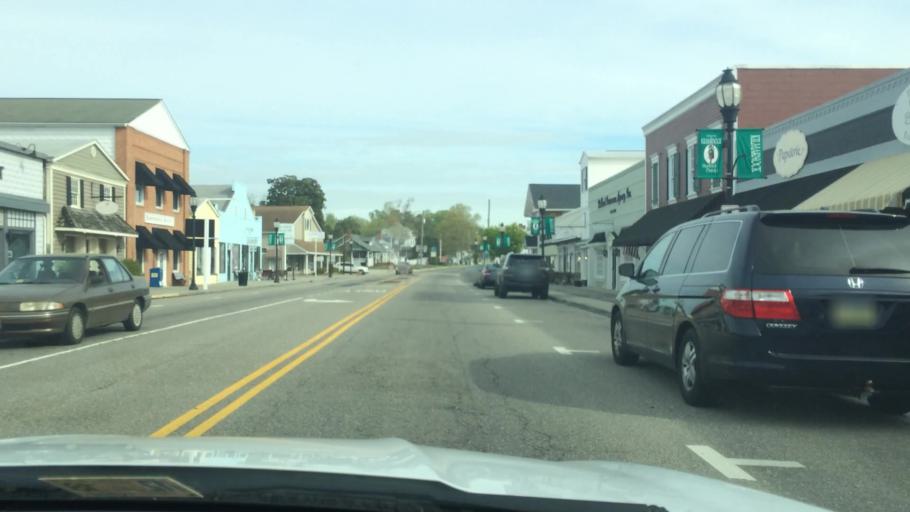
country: US
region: Virginia
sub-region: Lancaster County
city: Kilmarnock
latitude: 37.7114
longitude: -76.3805
